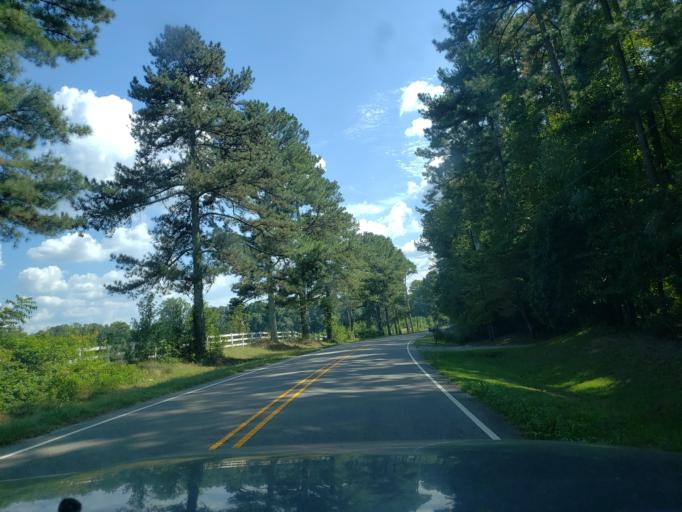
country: US
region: North Carolina
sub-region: Wake County
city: West Raleigh
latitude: 35.9216
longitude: -78.6853
